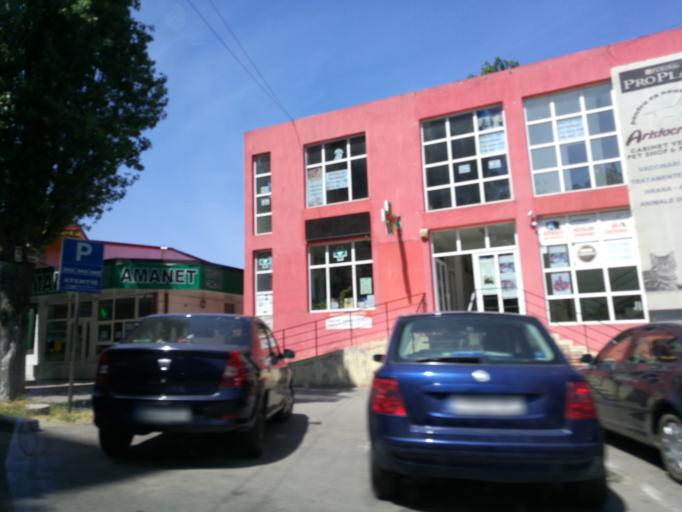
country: RO
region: Constanta
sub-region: Municipiul Constanta
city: Constanta
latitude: 44.2041
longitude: 28.6253
